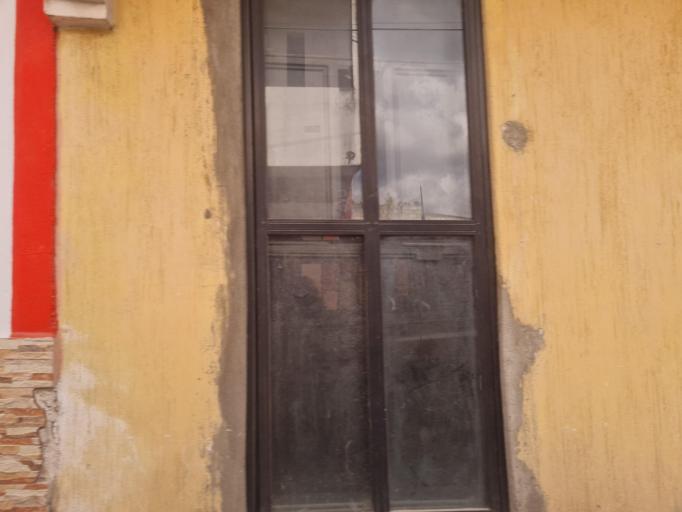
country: GT
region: Quetzaltenango
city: Quetzaltenango
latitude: 14.8333
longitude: -91.5302
